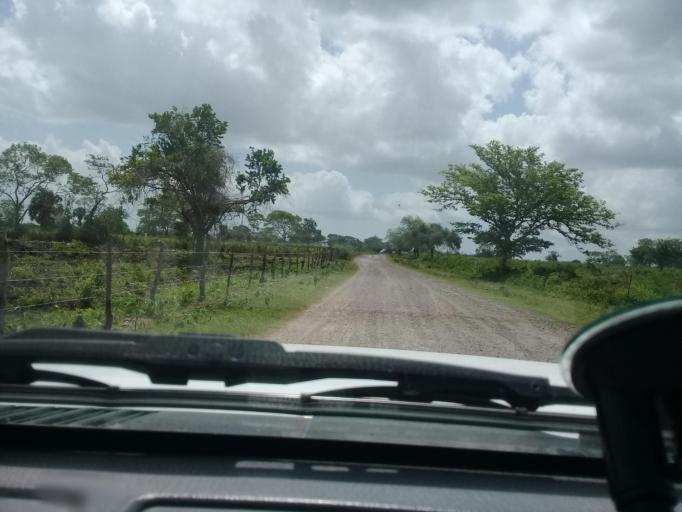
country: MX
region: Veracruz
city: Moralillo
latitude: 22.1598
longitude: -97.9951
